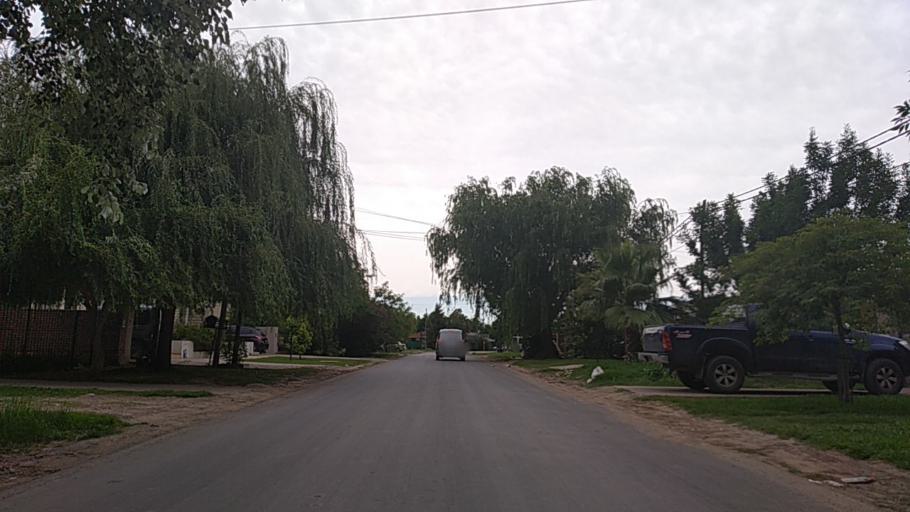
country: AR
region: Santa Fe
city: Funes
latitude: -32.9248
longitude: -60.7936
